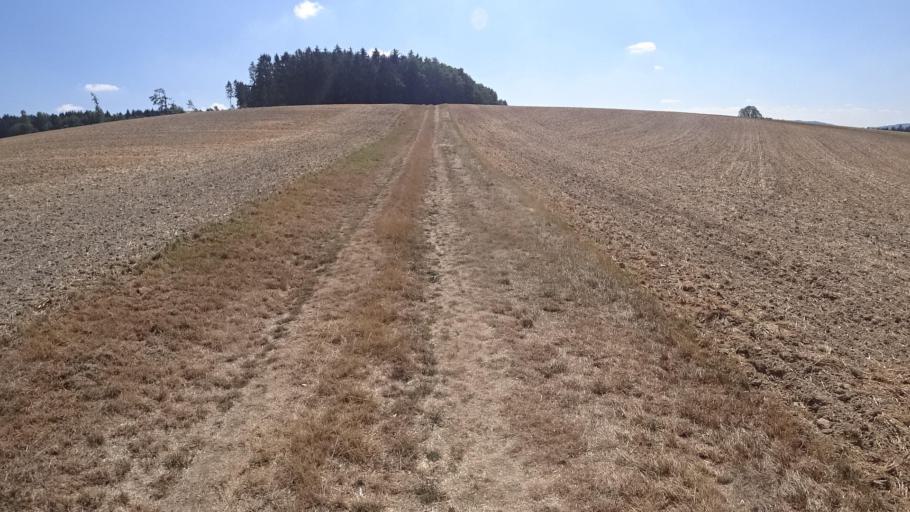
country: DE
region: Rheinland-Pfalz
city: Schonborn
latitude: 49.9575
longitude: 7.4610
